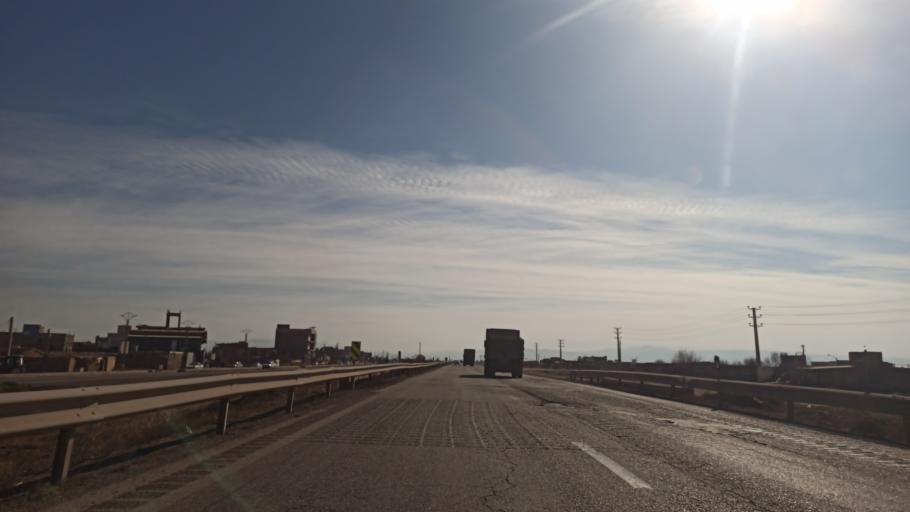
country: IR
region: Qazvin
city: Bu'in Zahra
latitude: 35.8502
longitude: 50.0607
